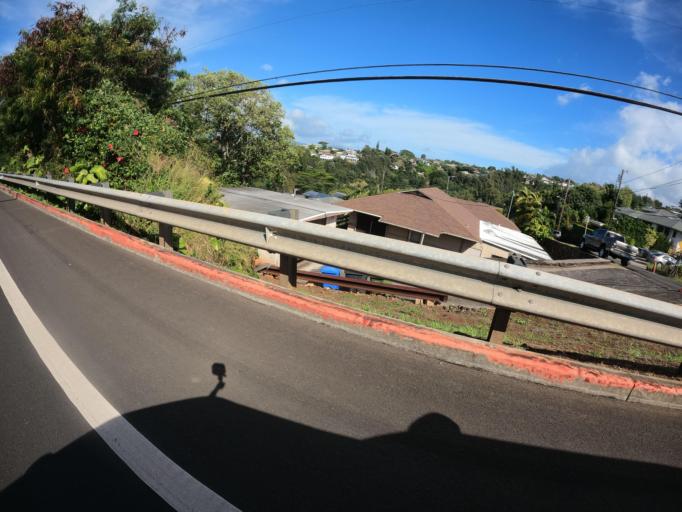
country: US
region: Hawaii
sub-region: Honolulu County
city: Halawa Heights
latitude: 21.3878
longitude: -157.9080
